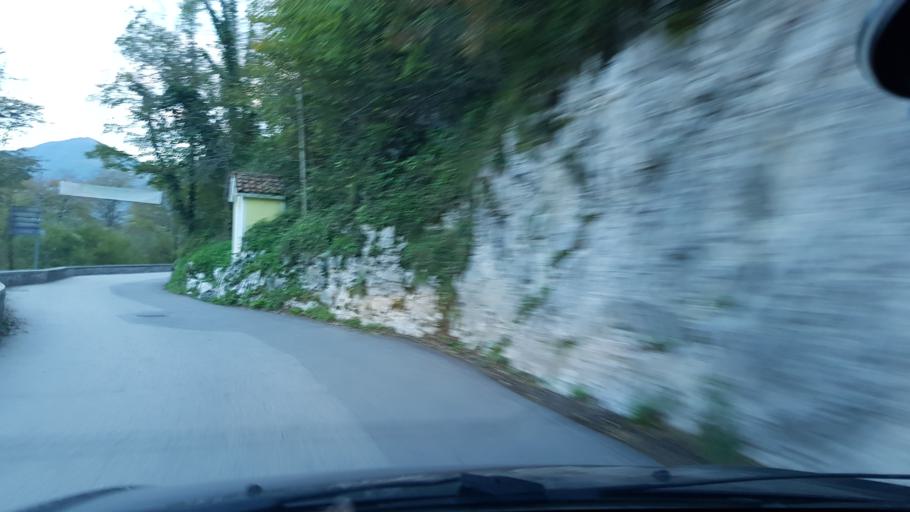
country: SI
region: Kobarid
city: Kobarid
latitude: 46.2483
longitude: 13.5858
